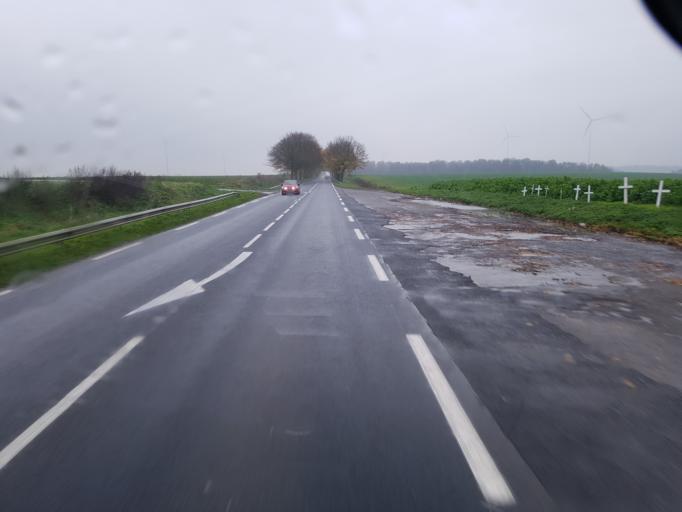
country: FR
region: Picardie
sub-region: Departement de l'Aisne
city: Saint-Quentin
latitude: 49.8785
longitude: 3.2682
